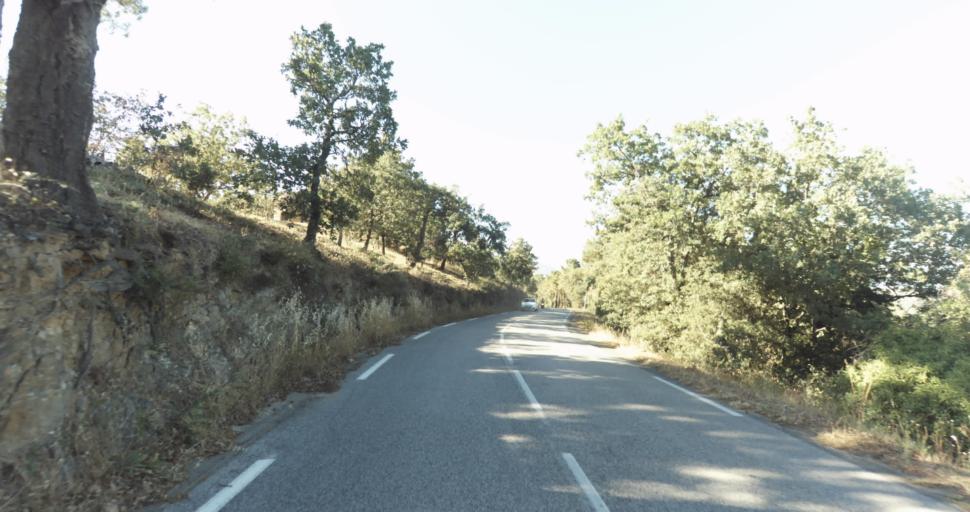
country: FR
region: Provence-Alpes-Cote d'Azur
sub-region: Departement du Var
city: Gassin
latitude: 43.2338
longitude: 6.5857
